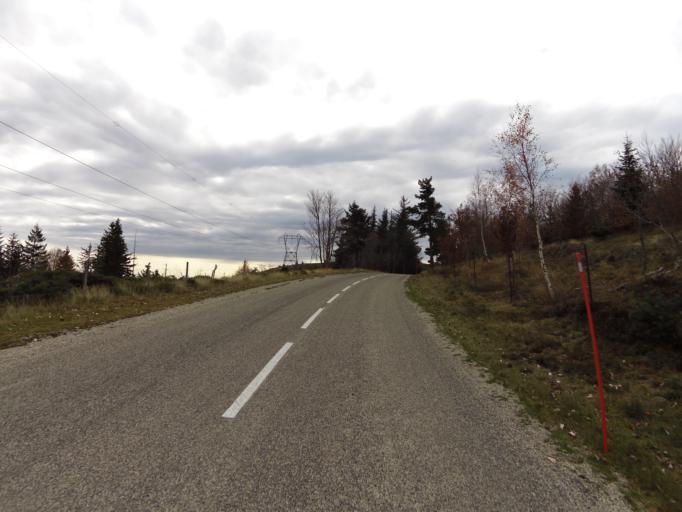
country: FR
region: Rhone-Alpes
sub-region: Departement de l'Ardeche
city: Les Vans
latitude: 44.5594
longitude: 4.0196
